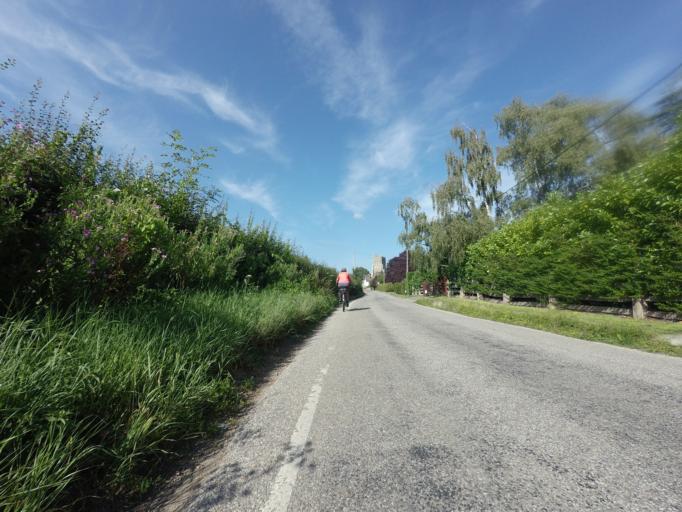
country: GB
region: England
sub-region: Kent
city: Tenterden
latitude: 51.0095
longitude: 0.7009
